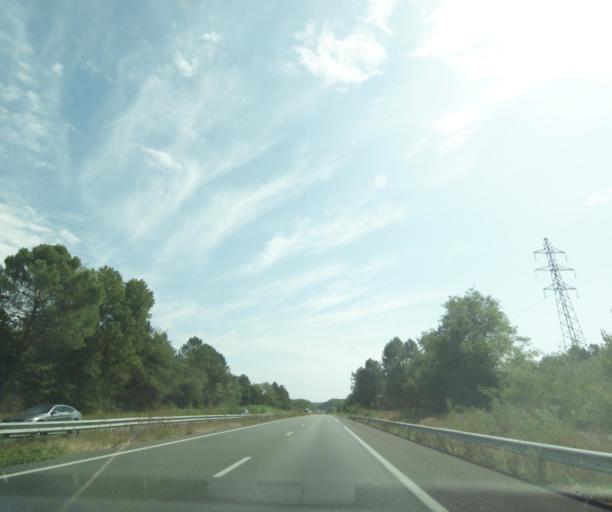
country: FR
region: Aquitaine
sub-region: Departement de la Gironde
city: Peujard
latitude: 45.0522
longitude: -0.4532
